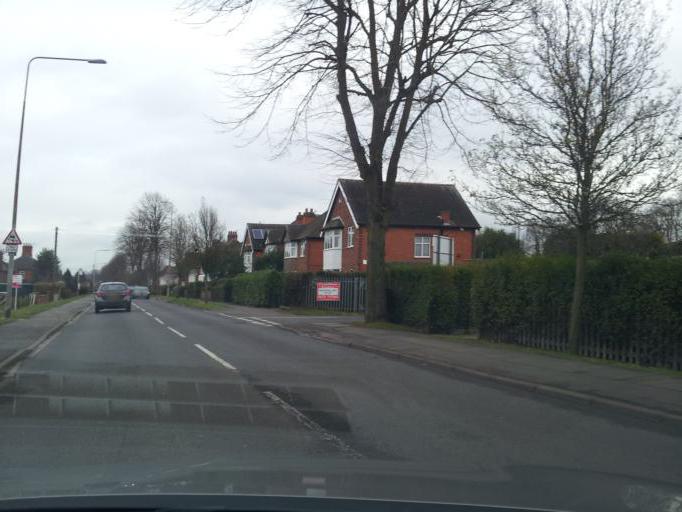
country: GB
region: England
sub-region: Lincolnshire
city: Barrowby
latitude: 52.9097
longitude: -0.6679
